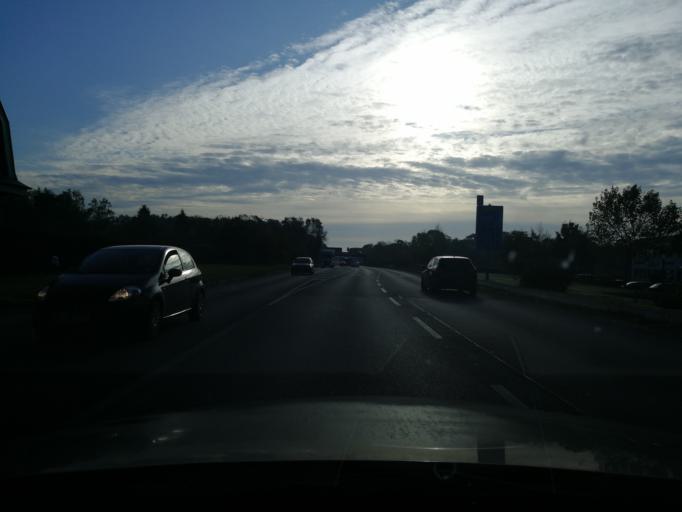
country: DE
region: North Rhine-Westphalia
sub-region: Regierungsbezirk Dusseldorf
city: Dusseldorf
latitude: 51.1654
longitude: 6.7649
